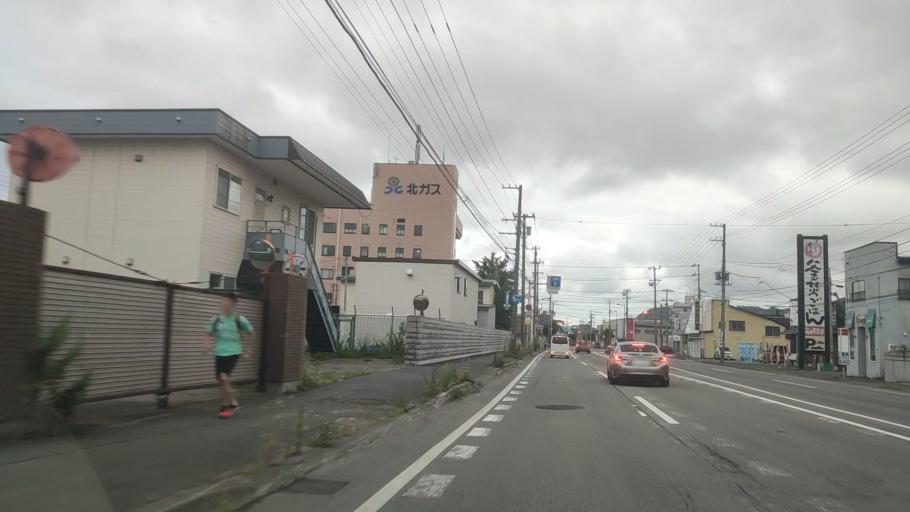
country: JP
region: Hokkaido
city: Hakodate
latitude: 41.7906
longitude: 140.7323
